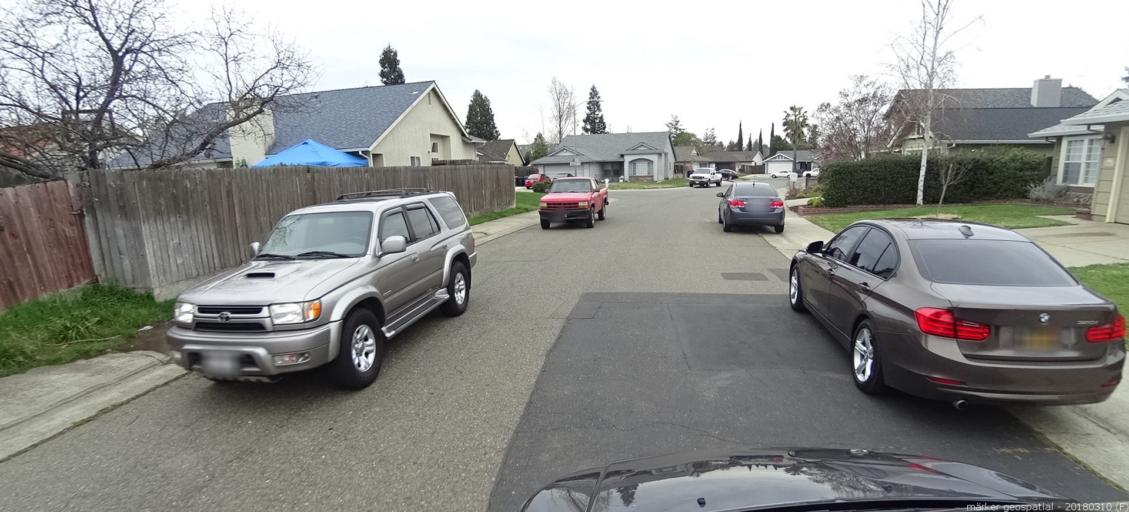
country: US
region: California
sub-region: Sacramento County
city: Vineyard
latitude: 38.4658
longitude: -121.3650
